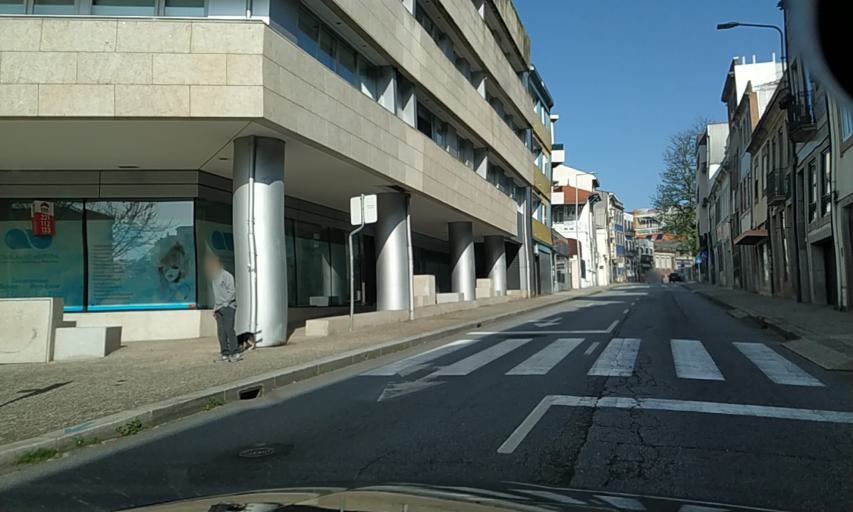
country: PT
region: Porto
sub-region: Porto
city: Porto
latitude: 41.1586
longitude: -8.6234
